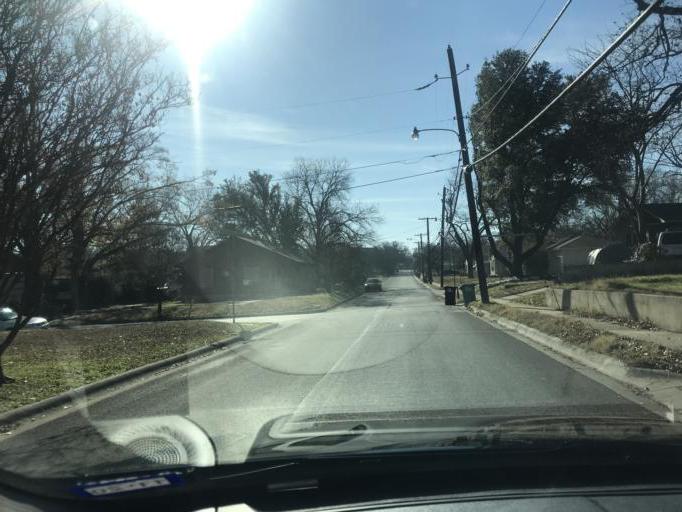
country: US
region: Texas
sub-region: Denton County
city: Denton
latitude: 33.2182
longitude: -97.1540
